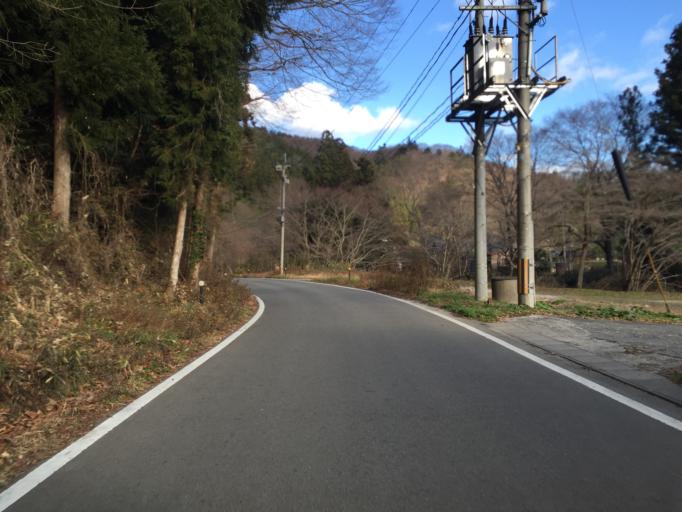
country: JP
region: Fukushima
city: Funehikimachi-funehiki
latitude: 37.2341
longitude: 140.6932
